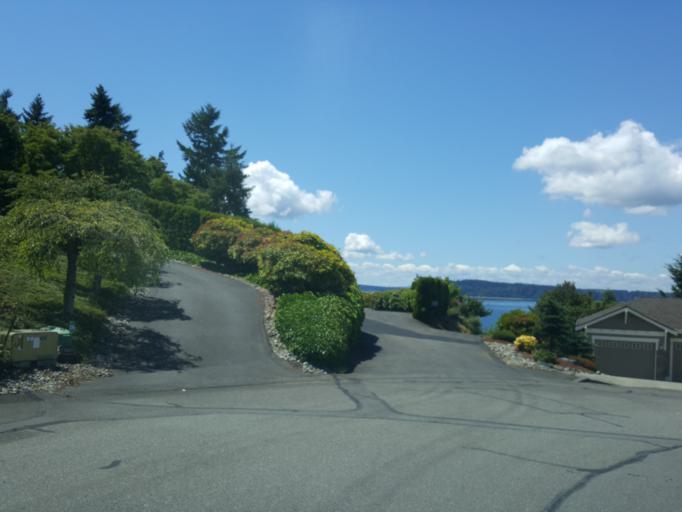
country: US
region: Washington
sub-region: Pierce County
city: University Place
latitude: 47.2141
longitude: -122.5739
